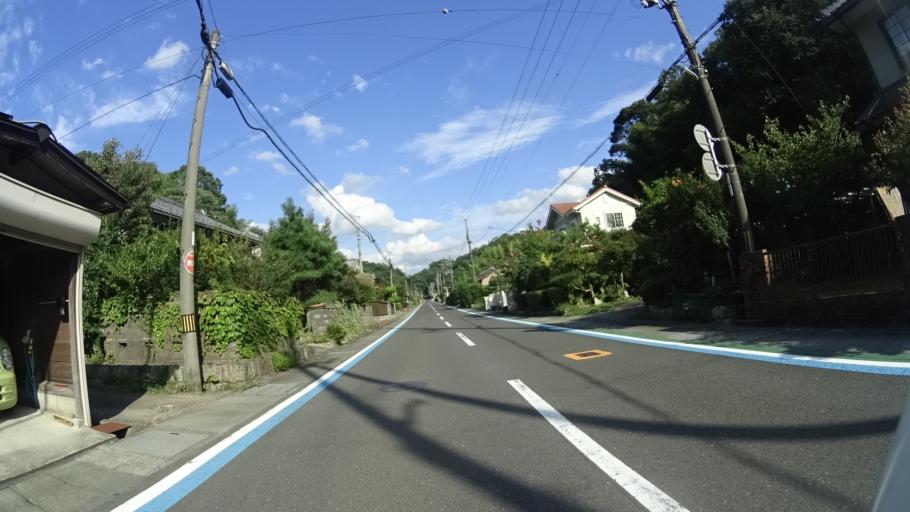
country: JP
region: Kyoto
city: Maizuru
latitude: 35.4819
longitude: 135.3521
